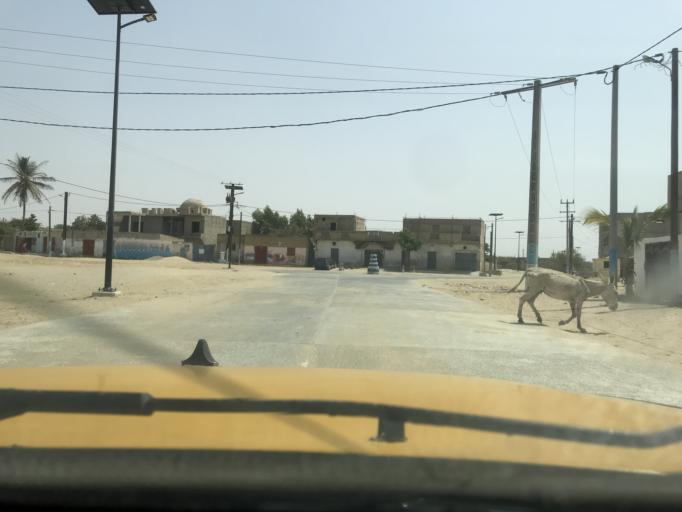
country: SN
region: Saint-Louis
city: Saint-Louis
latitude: 16.0195
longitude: -16.4467
